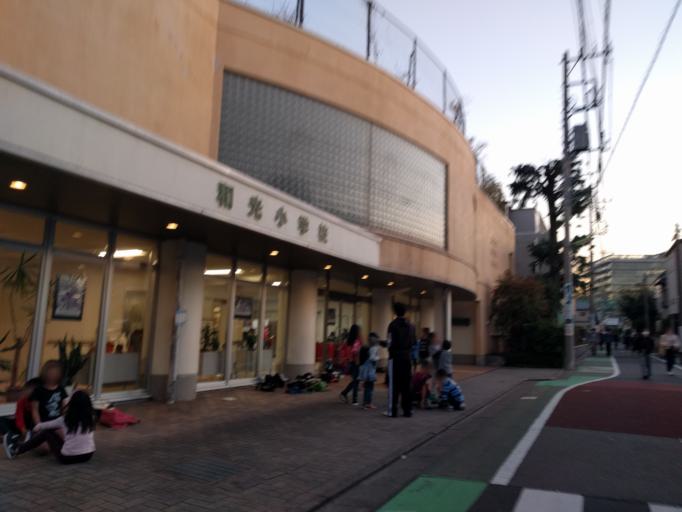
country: JP
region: Tokyo
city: Tokyo
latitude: 35.6444
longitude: 139.6352
